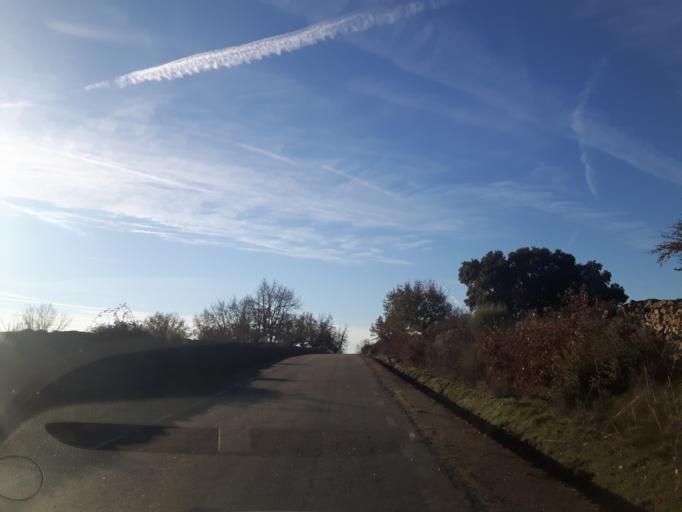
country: ES
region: Castille and Leon
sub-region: Provincia de Salamanca
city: Cerralbo
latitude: 40.9417
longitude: -6.6191
